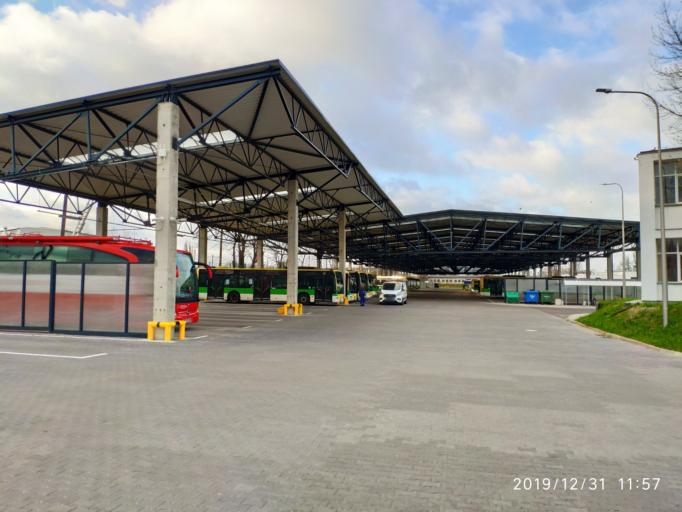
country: PL
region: Lubusz
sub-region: Zielona Gora
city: Zielona Gora
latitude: 51.9505
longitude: 15.4851
